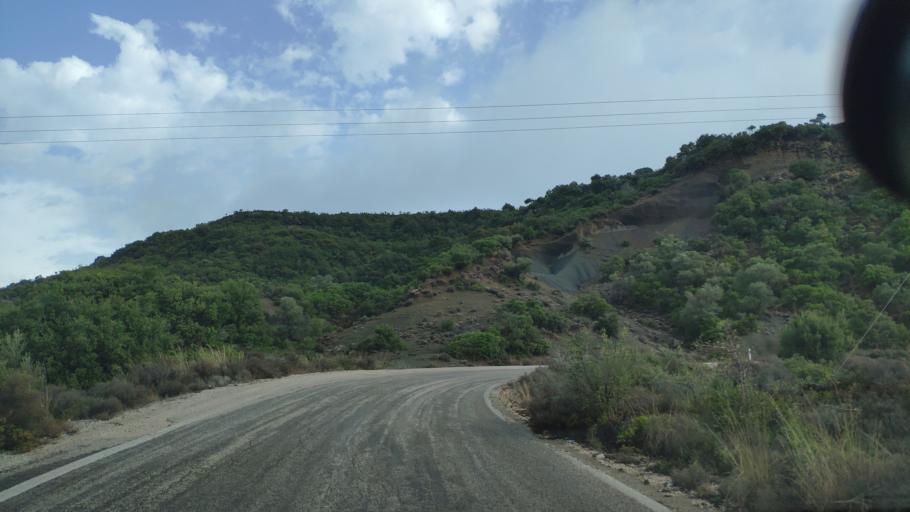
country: GR
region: West Greece
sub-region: Nomos Aitolias kai Akarnanias
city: Sardinia
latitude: 38.8758
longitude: 21.2566
